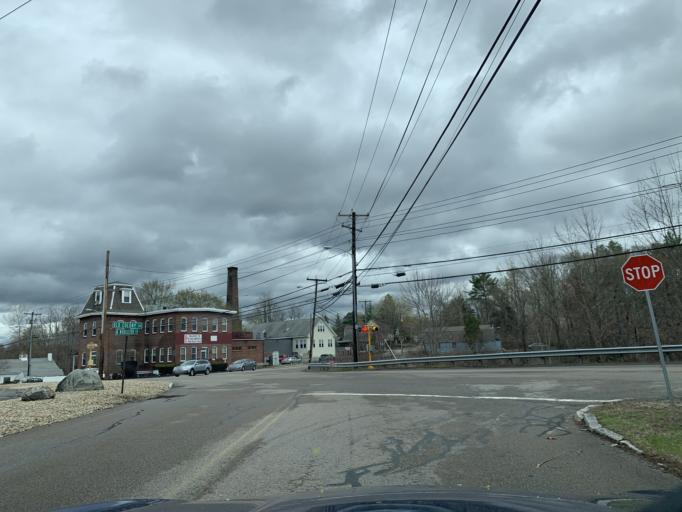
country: US
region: Massachusetts
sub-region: Bristol County
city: Norton
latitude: 41.9505
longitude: -71.2283
